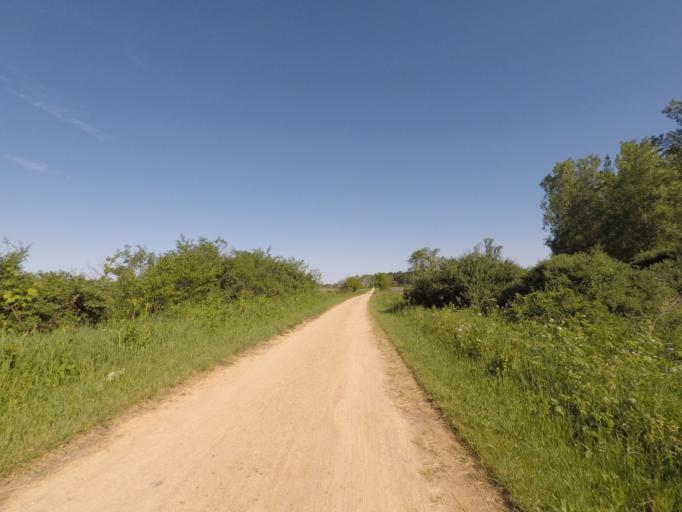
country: US
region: Wisconsin
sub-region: Dane County
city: Verona
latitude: 42.9815
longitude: -89.5608
